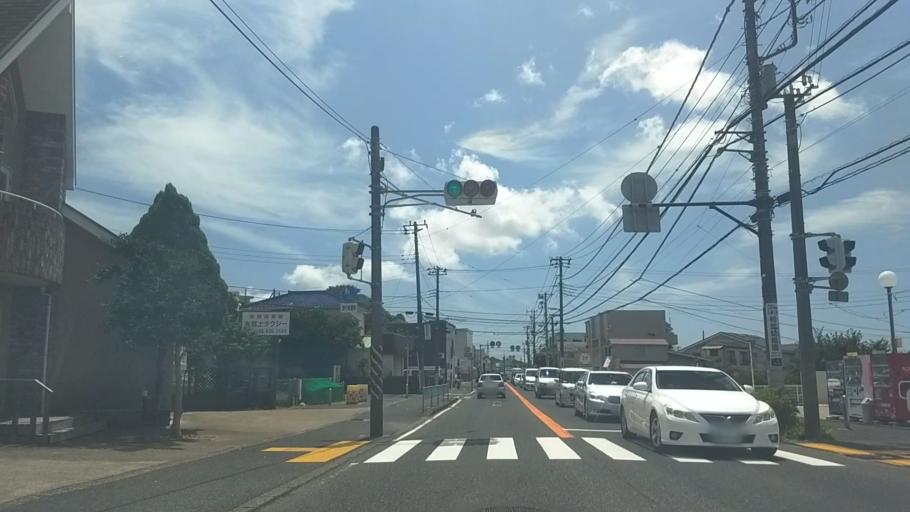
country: JP
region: Kanagawa
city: Yokosuka
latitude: 35.2225
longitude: 139.6432
